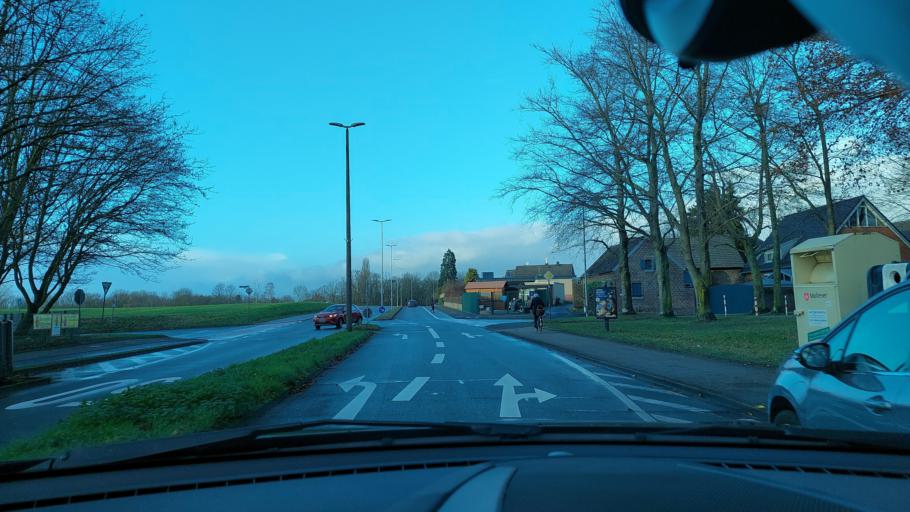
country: DE
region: North Rhine-Westphalia
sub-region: Regierungsbezirk Dusseldorf
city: Dormagen
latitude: 51.0647
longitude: 6.8079
